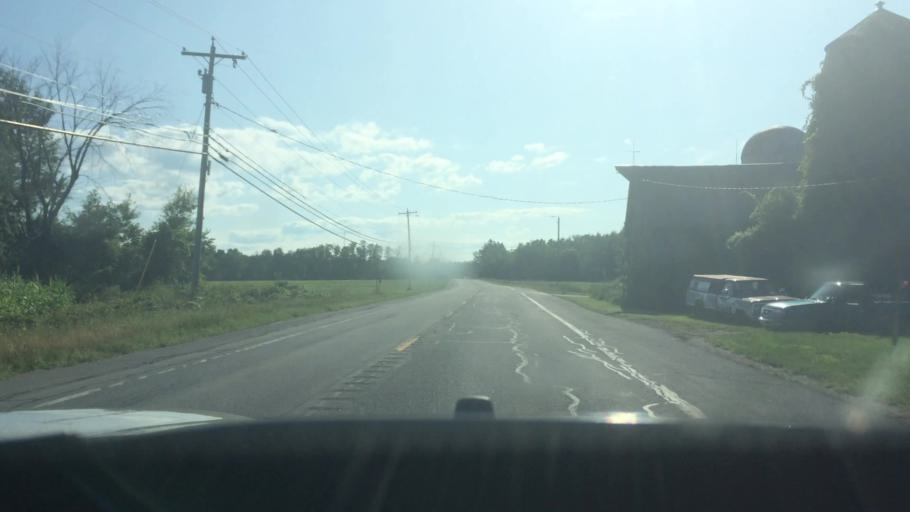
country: US
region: New York
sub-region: Franklin County
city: Malone
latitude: 44.8272
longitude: -74.3425
